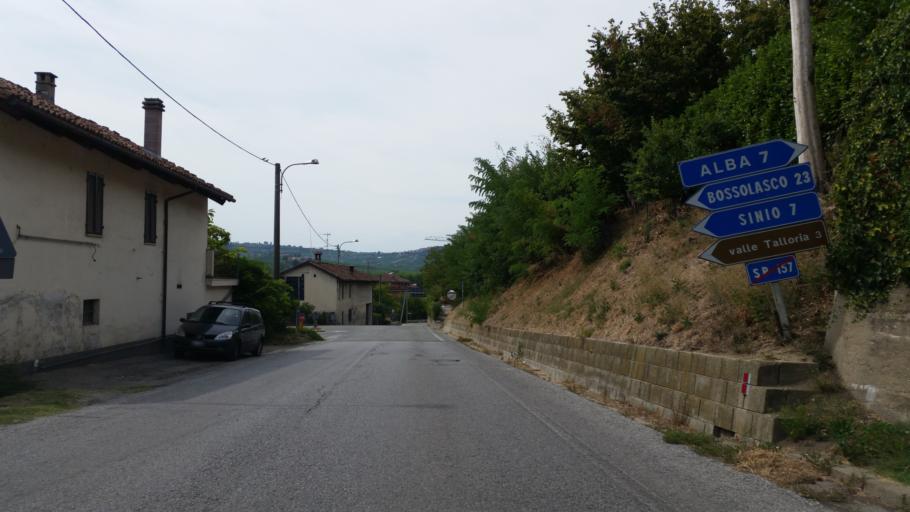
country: IT
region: Piedmont
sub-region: Provincia di Cuneo
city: Grinzane Cavour
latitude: 44.6540
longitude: 7.9839
